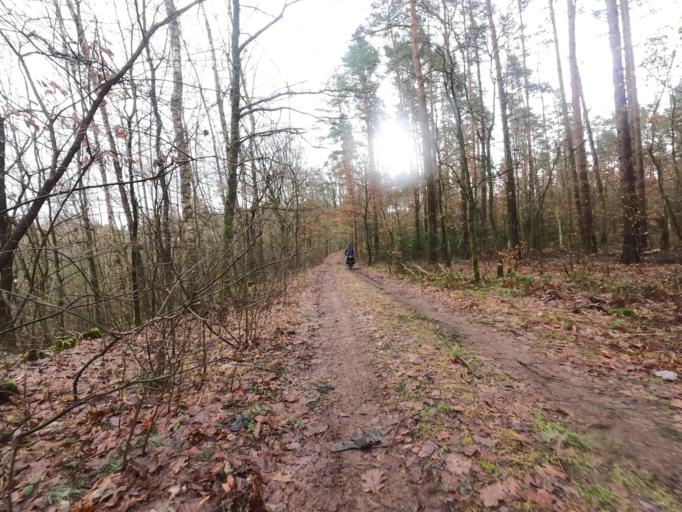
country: PL
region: Greater Poland Voivodeship
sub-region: Powiat pilski
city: Smilowo
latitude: 53.1136
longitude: 16.9193
